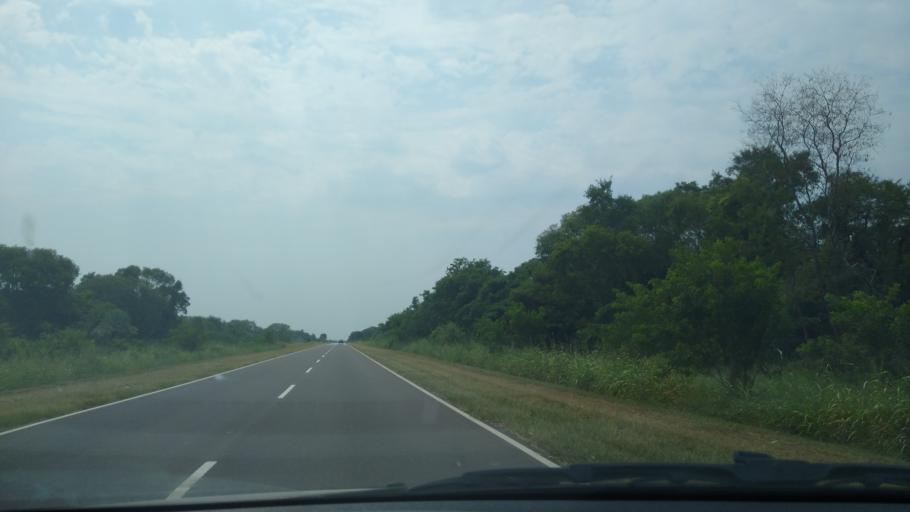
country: AR
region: Chaco
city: La Eduvigis
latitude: -27.0123
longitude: -58.9699
